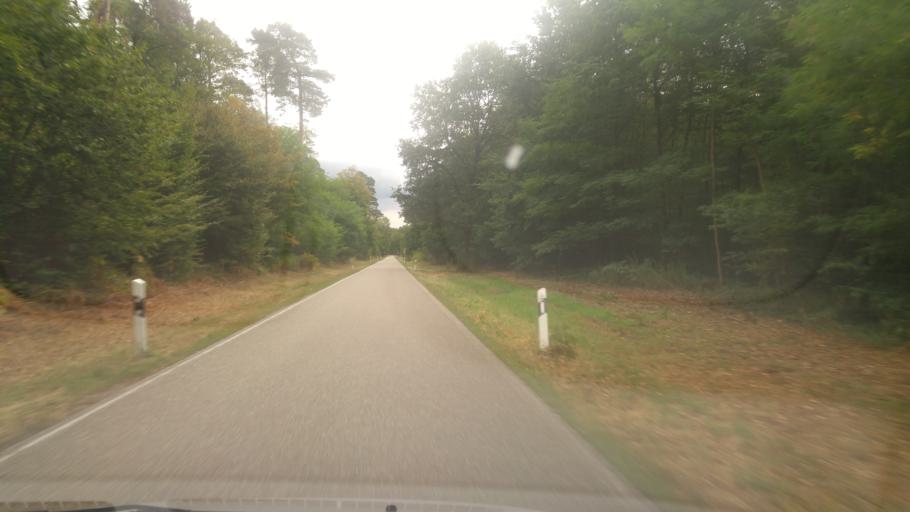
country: DE
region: Rheinland-Pfalz
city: Scheibenhardt
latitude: 48.9948
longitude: 8.0869
